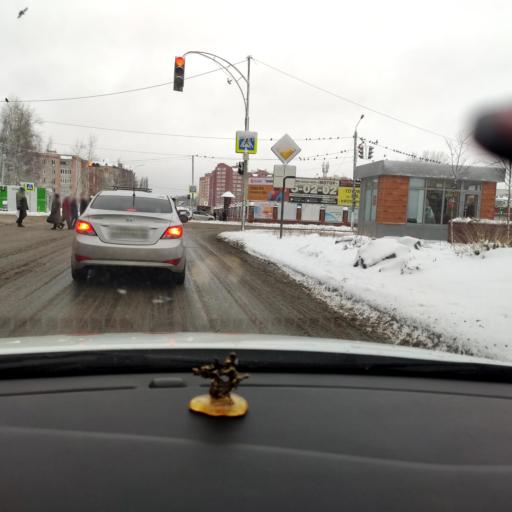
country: RU
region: Tatarstan
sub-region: Zelenodol'skiy Rayon
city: Zelenodolsk
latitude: 55.8561
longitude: 48.5607
